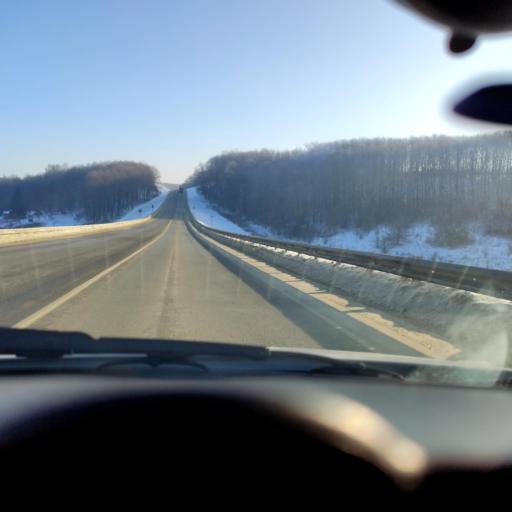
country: RU
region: Kursk
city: Tim
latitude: 51.6508
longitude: 36.9802
